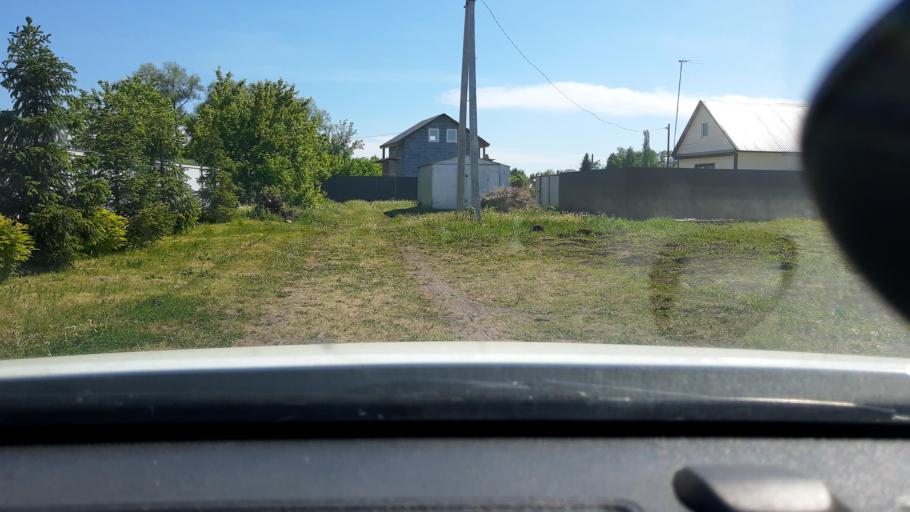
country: RU
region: Bashkortostan
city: Avdon
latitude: 54.5038
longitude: 55.8152
